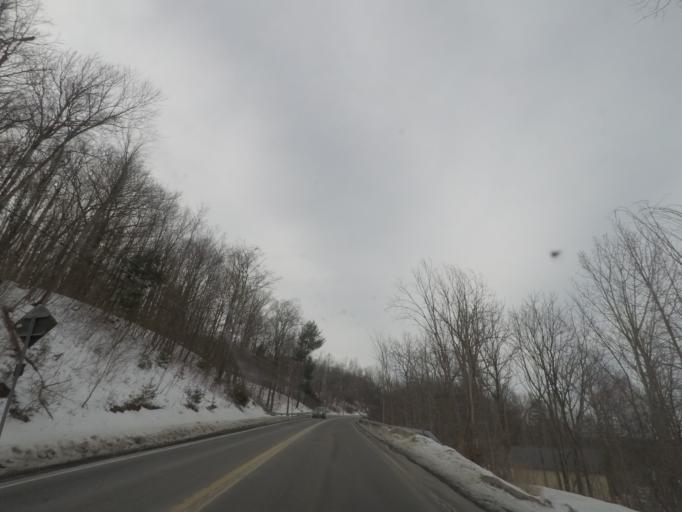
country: US
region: New York
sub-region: Albany County
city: Altamont
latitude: 42.7013
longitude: -74.0355
